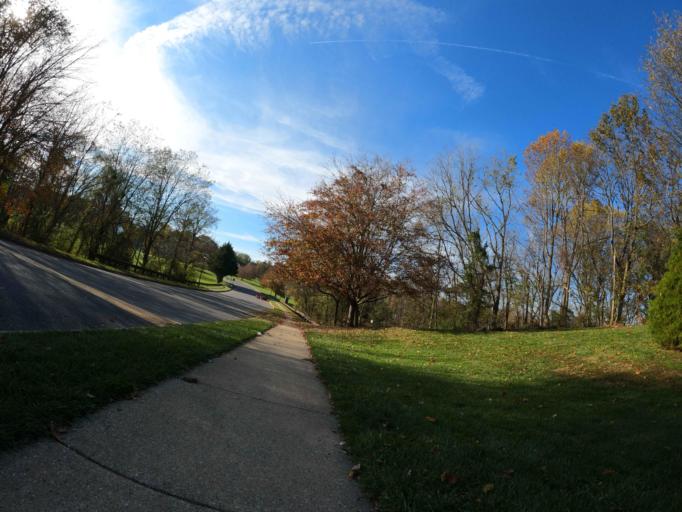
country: US
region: Maryland
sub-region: Carroll County
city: Sykesville
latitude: 39.3734
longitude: -76.9805
